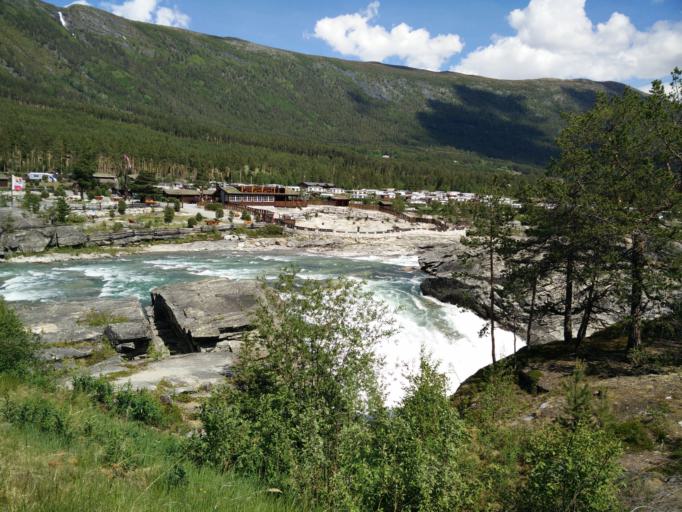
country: NO
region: Oppland
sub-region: Skjak
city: Bismo
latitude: 61.9152
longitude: 8.0930
